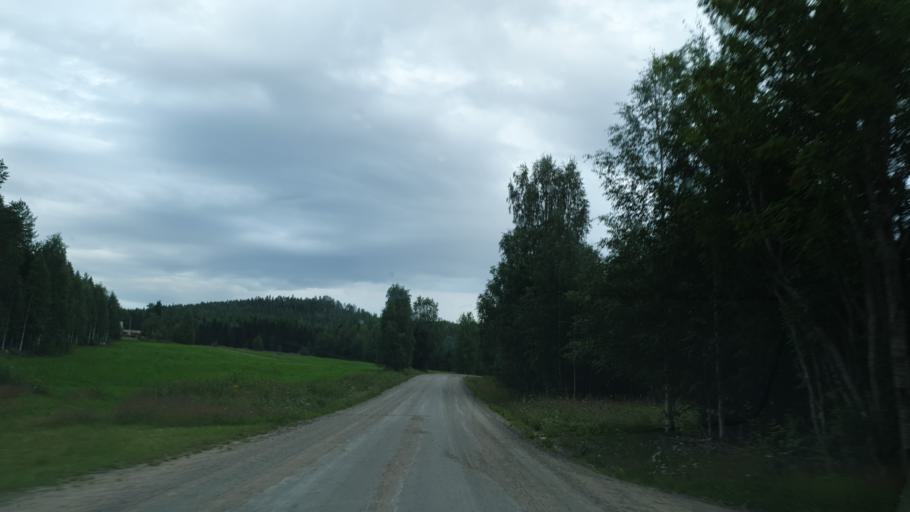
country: FI
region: Kainuu
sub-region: Kehys-Kainuu
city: Kuhmo
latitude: 64.2055
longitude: 29.3724
